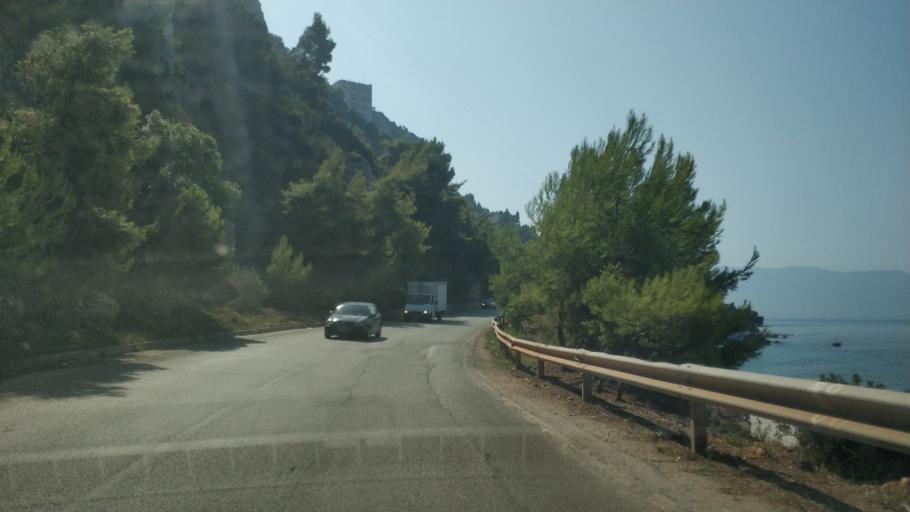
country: AL
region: Vlore
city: Vlore
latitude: 40.4091
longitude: 19.4805
